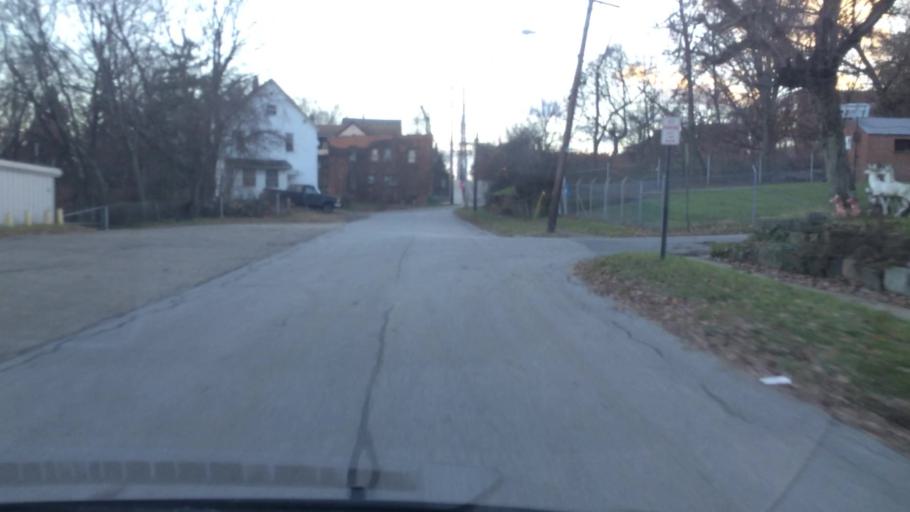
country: US
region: Ohio
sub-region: Summit County
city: Akron
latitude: 41.0841
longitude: -81.4981
